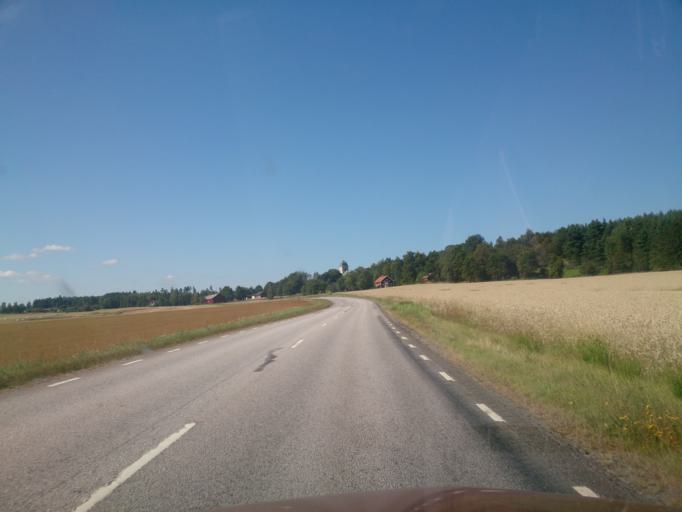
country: SE
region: OEstergoetland
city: Lindo
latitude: 58.5809
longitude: 16.3290
